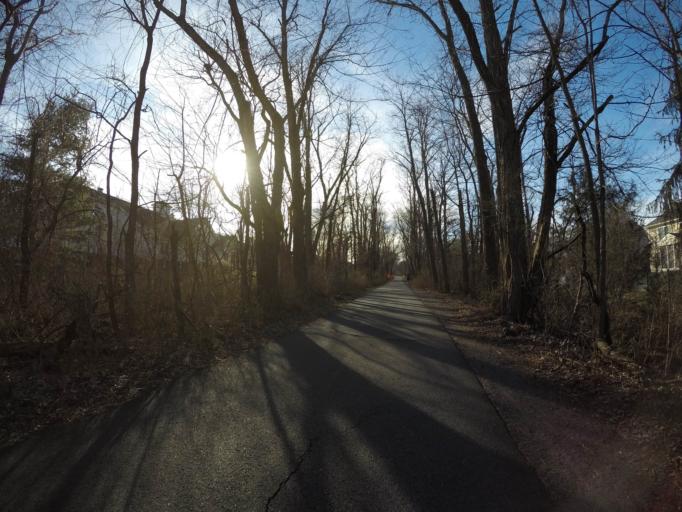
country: US
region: Virginia
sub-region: Loudoun County
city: Leesburg
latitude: 39.1129
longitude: -77.5771
